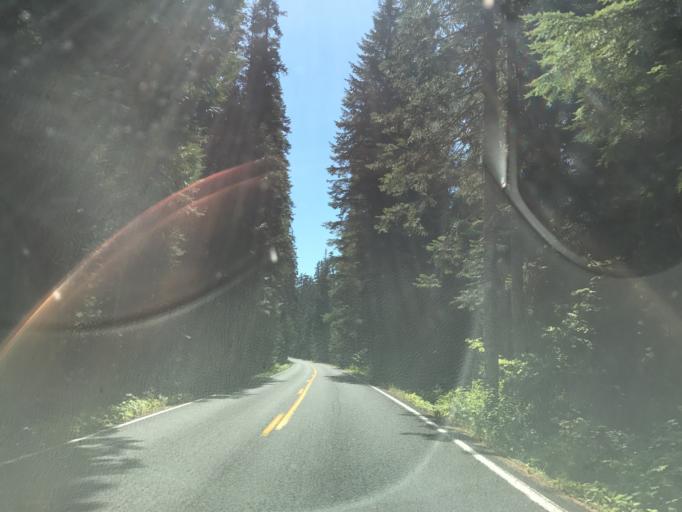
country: US
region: Washington
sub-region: Pierce County
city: Buckley
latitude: 46.7919
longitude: -121.5546
